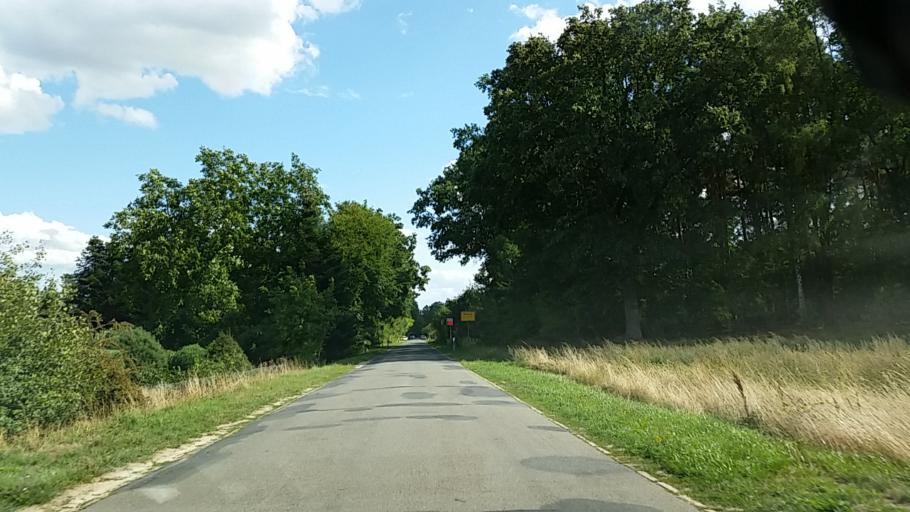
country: DE
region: Lower Saxony
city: Natendorf
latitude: 53.1128
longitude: 10.4473
